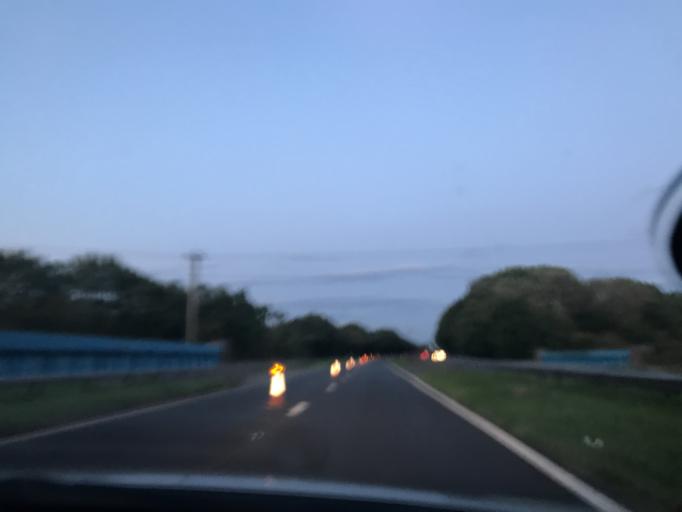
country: GB
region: England
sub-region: Cheshire West and Chester
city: Hartford
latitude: 53.2388
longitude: -2.5493
